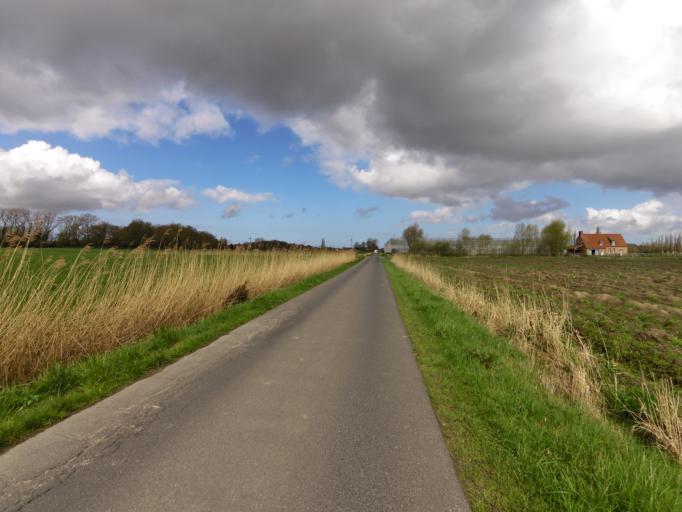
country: BE
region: Flanders
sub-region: Provincie West-Vlaanderen
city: Gistel
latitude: 51.1480
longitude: 2.9805
